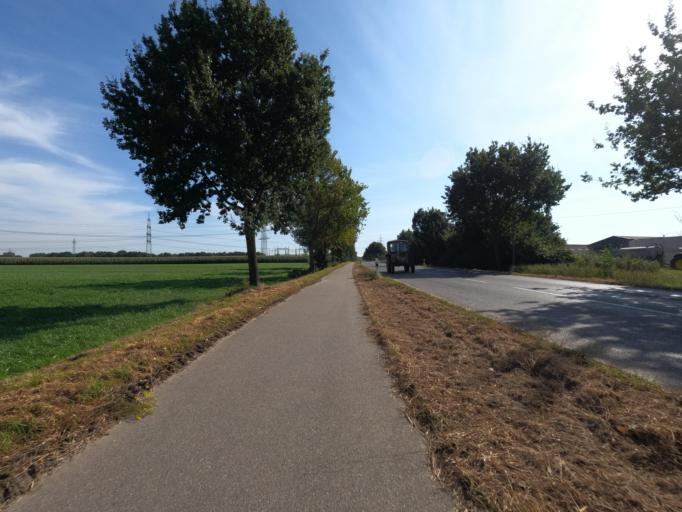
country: DE
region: North Rhine-Westphalia
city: Baesweiler
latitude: 50.9171
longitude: 6.2101
